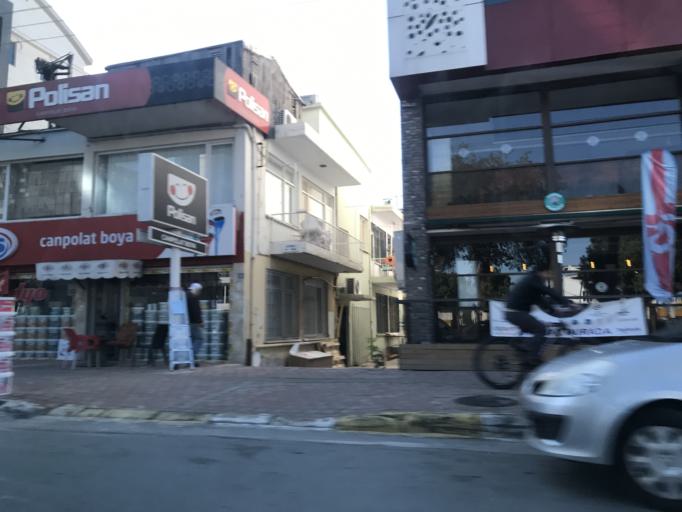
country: TR
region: Antalya
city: Antalya
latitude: 36.8994
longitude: 30.7064
